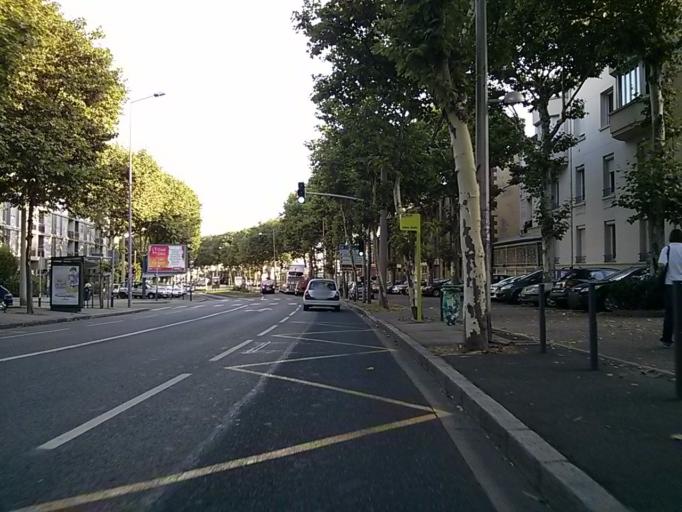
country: FR
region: Rhone-Alpes
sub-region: Departement de la Loire
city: Saint-Etienne
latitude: 45.4458
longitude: 4.3978
